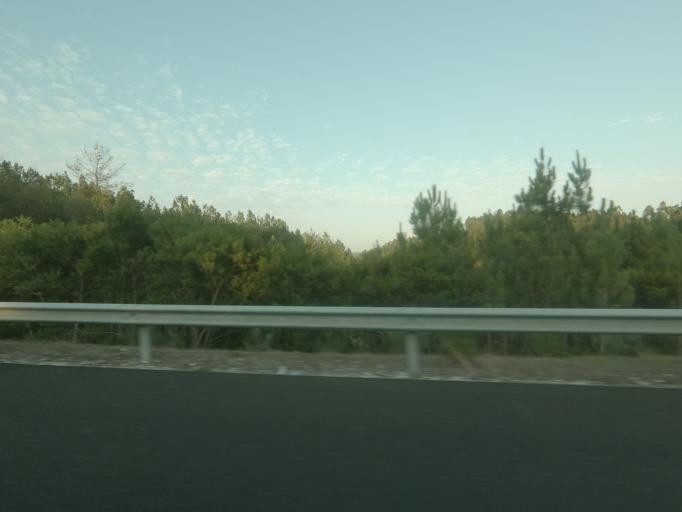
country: PT
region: Leiria
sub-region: Leiria
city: Caranguejeira
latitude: 39.7862
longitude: -8.7369
